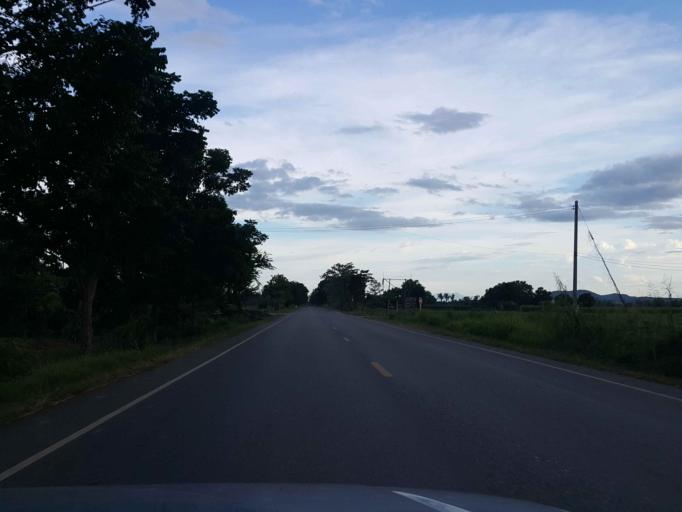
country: TH
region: Sukhothai
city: Sawankhalok
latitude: 17.3668
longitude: 99.7416
